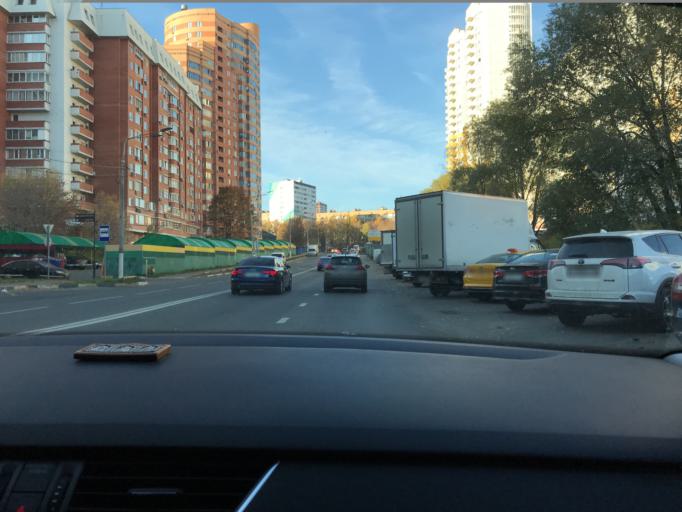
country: RU
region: Moscow
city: Khimki
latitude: 55.8847
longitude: 37.4276
